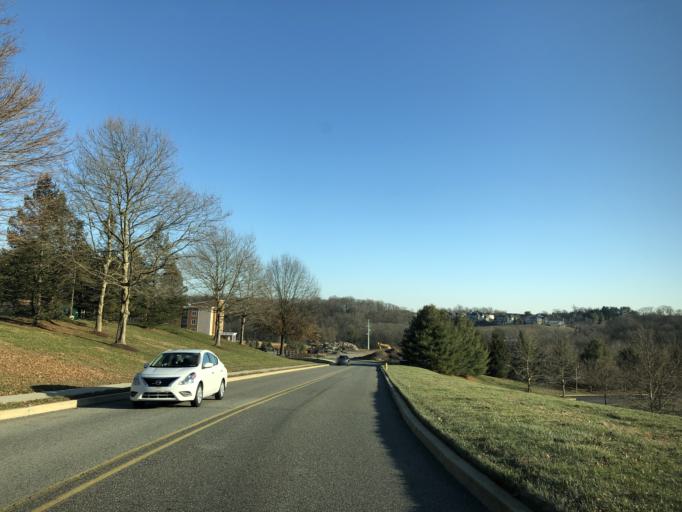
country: US
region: Pennsylvania
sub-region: Delaware County
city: Chester Heights
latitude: 39.8785
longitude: -75.5195
